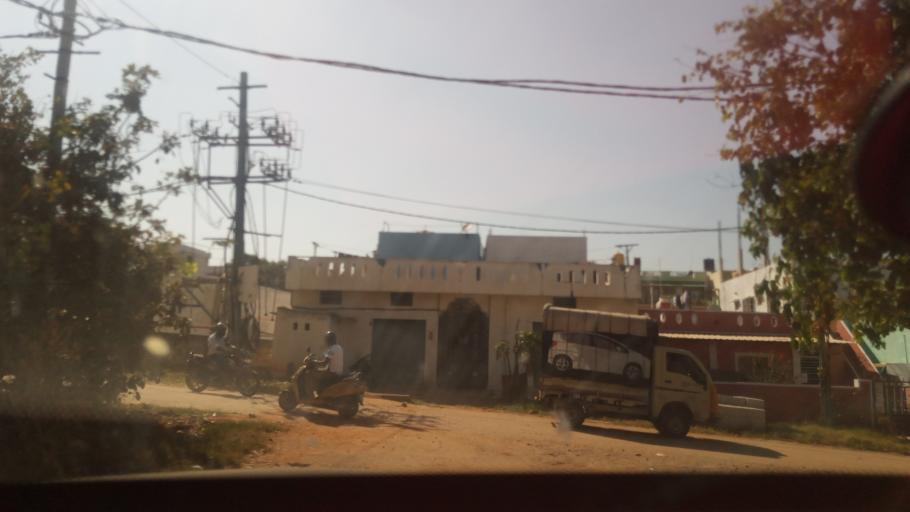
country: IN
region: Karnataka
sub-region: Bangalore Rural
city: Nelamangala
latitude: 13.0409
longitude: 77.4967
